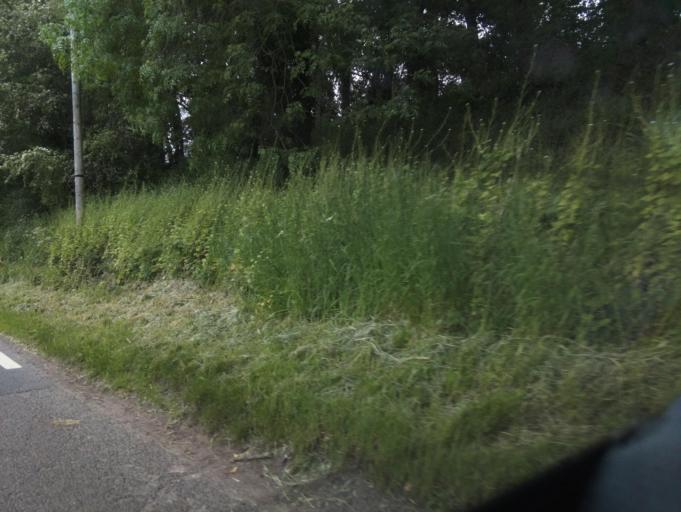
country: GB
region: England
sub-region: Herefordshire
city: Yatton
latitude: 51.9538
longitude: -2.5315
